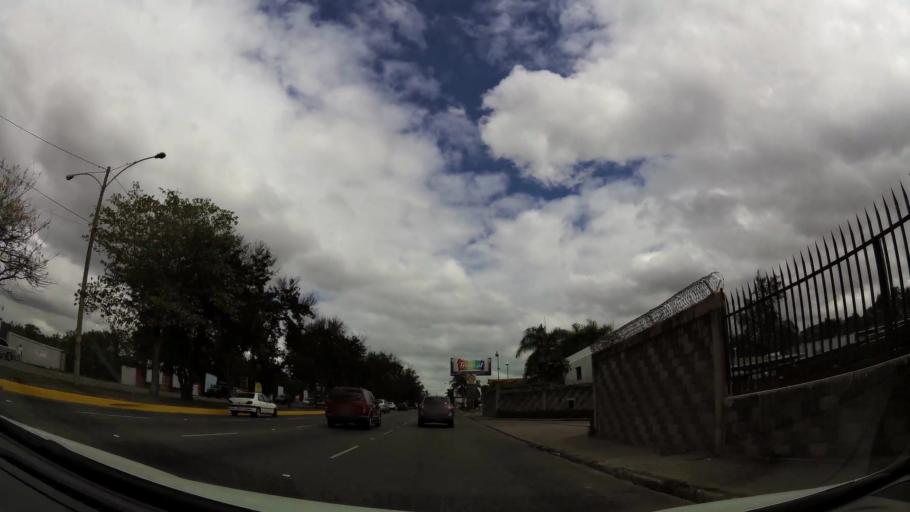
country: DO
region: Nacional
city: Bella Vista
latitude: 18.4683
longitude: -69.9683
